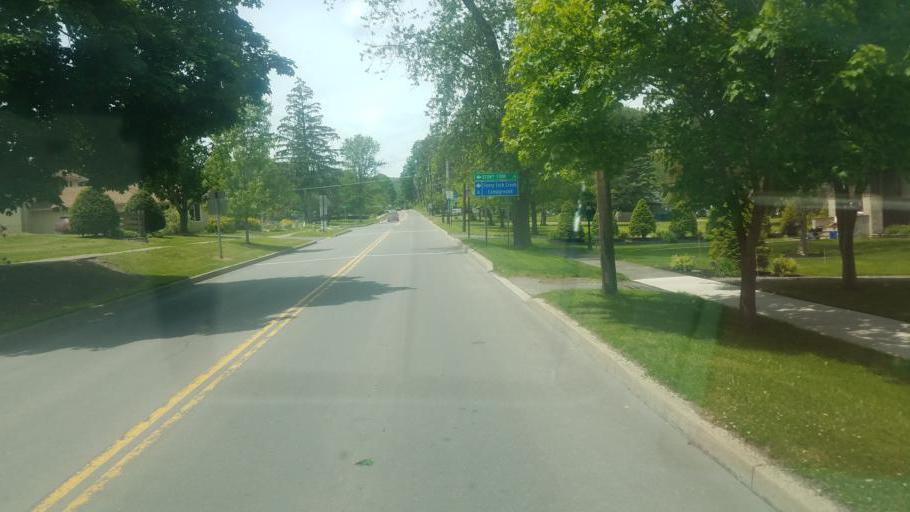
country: US
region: Pennsylvania
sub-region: Tioga County
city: Wellsboro
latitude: 41.7437
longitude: -77.3129
